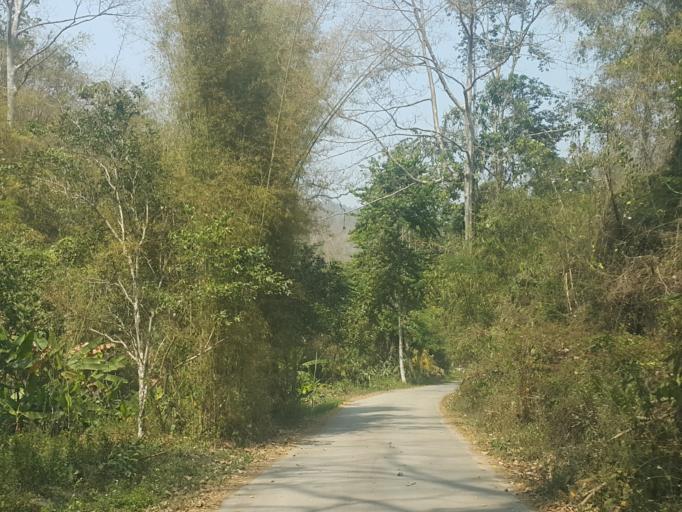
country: TH
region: Chiang Mai
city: Hang Dong
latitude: 18.7315
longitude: 98.8294
